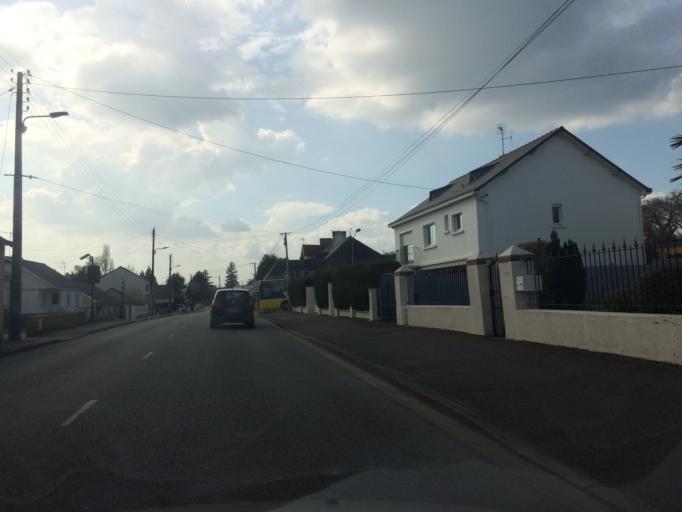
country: FR
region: Pays de la Loire
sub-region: Departement de la Loire-Atlantique
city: Blain
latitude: 47.4781
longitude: -1.7715
